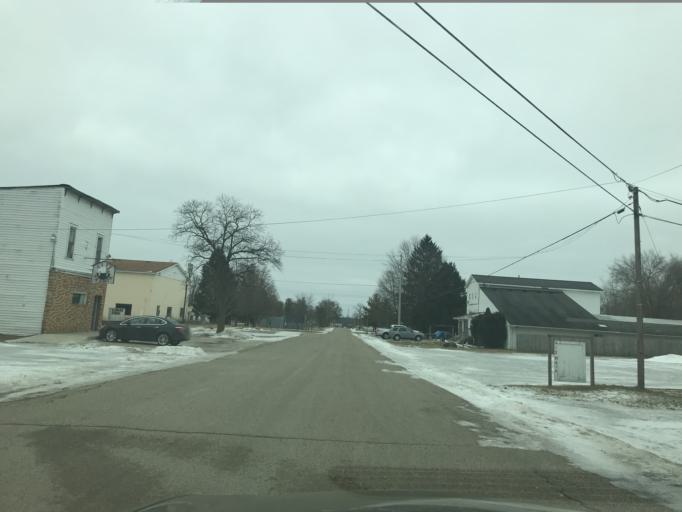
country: US
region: Michigan
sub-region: Jackson County
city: Brooklyn
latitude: 42.0699
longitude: -84.3317
